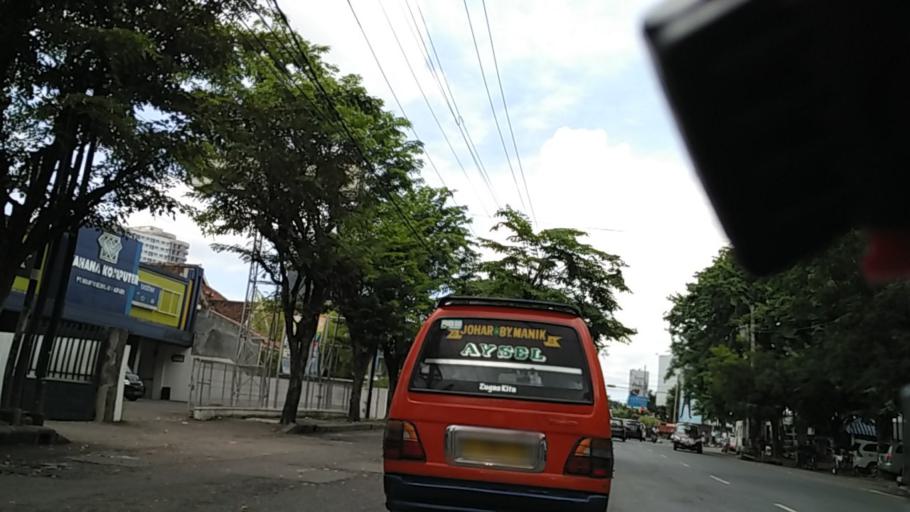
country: ID
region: Central Java
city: Semarang
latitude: -6.9956
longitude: 110.4320
